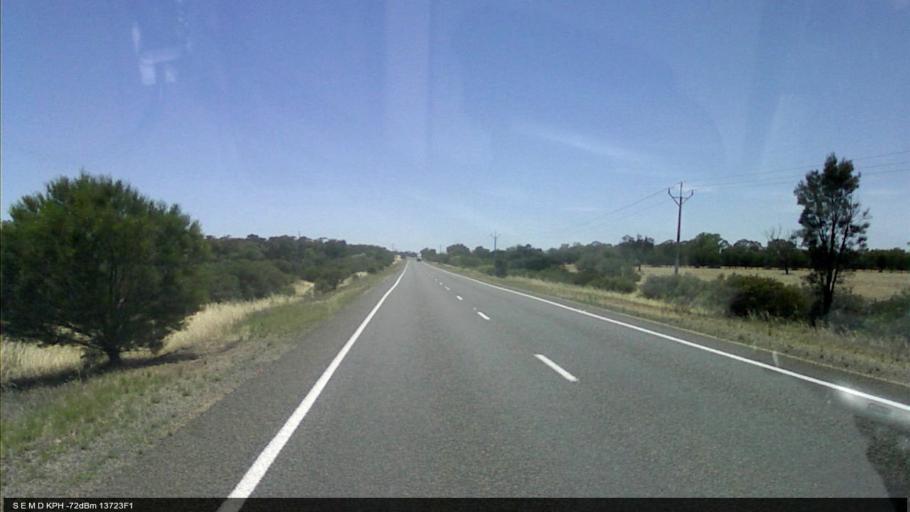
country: AU
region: New South Wales
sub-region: Wentworth
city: Gol Gol
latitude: -34.5215
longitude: 142.8204
